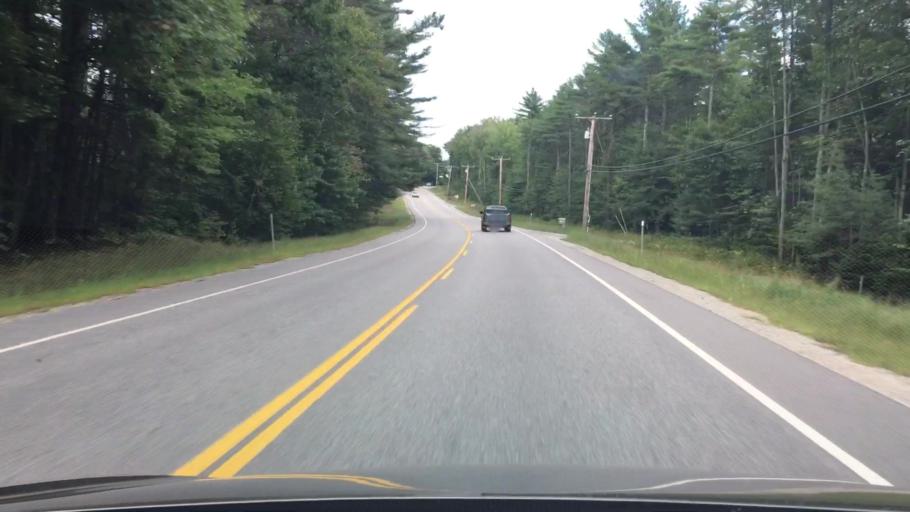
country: US
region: Maine
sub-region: Oxford County
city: Fryeburg
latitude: 43.9929
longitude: -71.0419
